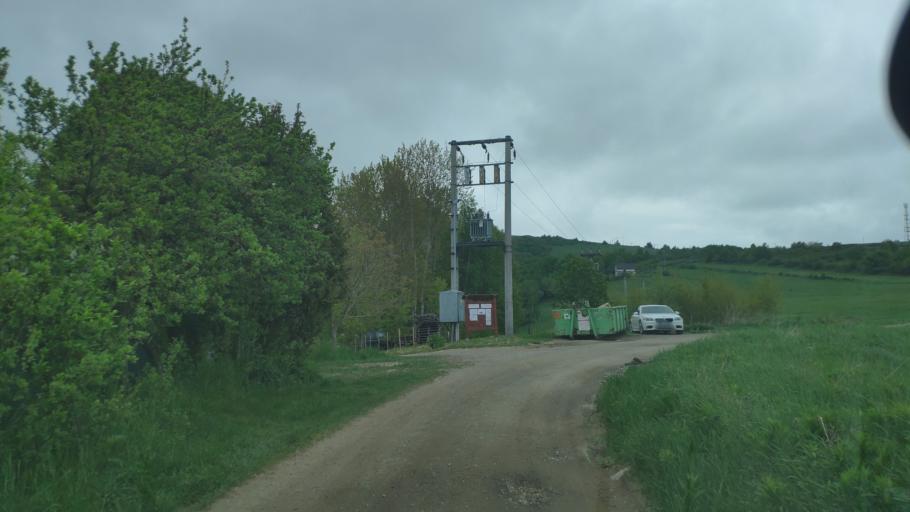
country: SK
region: Kosicky
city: Kosice
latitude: 48.7600
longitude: 21.2001
